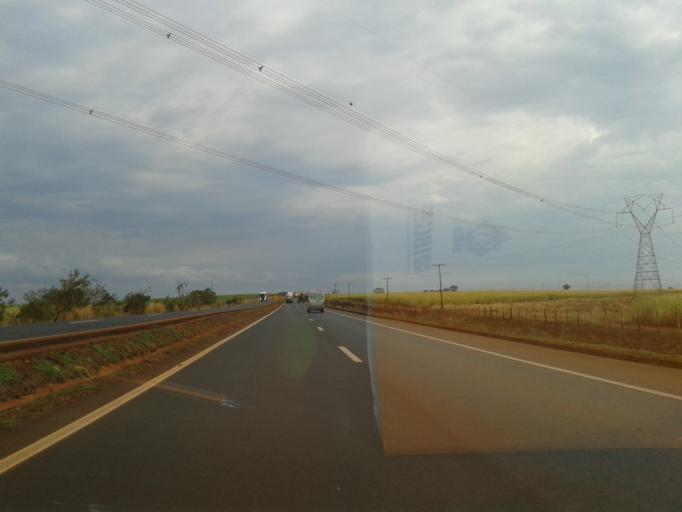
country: BR
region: Minas Gerais
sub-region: Centralina
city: Centralina
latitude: -18.5068
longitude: -49.1891
